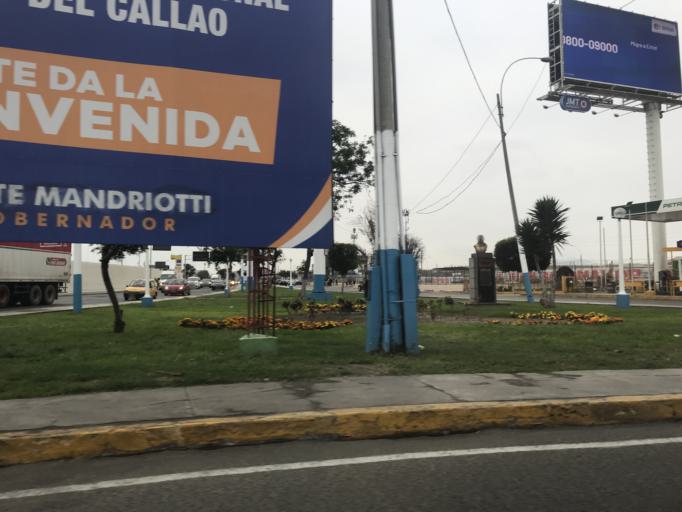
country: PE
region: Callao
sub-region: Callao
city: Callao
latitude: -12.0213
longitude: -77.1060
